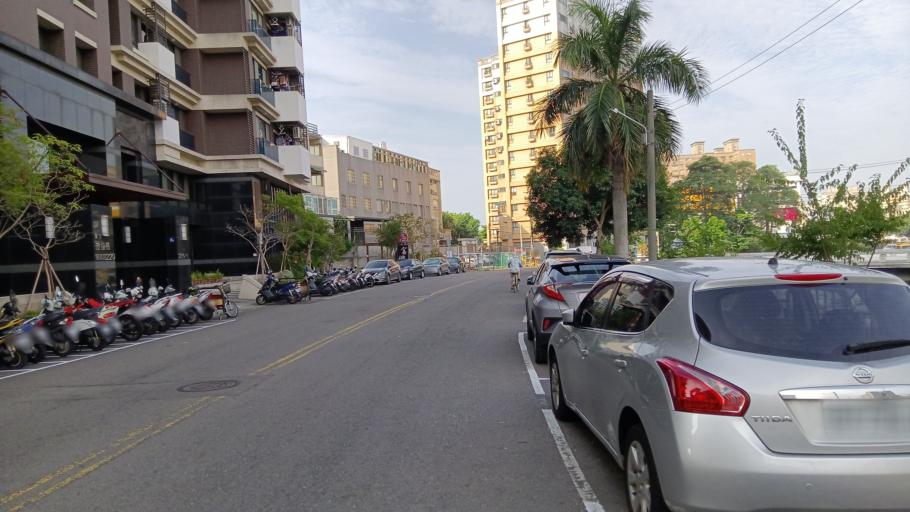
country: TW
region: Taiwan
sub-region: Taichung City
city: Taichung
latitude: 24.1174
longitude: 120.6560
